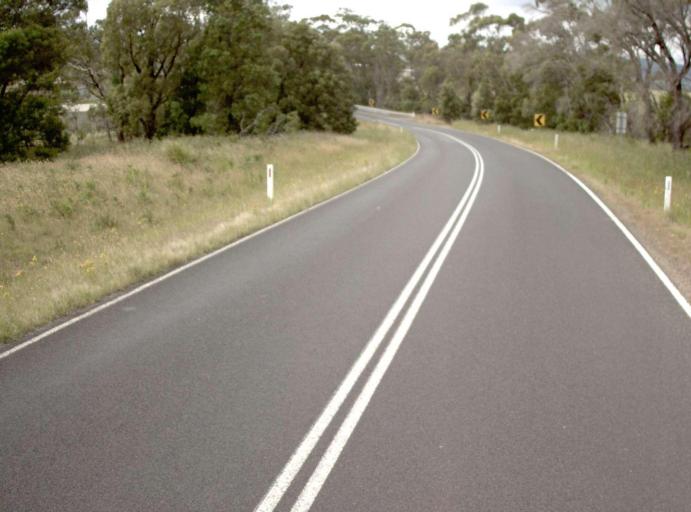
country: AU
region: Victoria
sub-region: Latrobe
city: Moe
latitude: -38.1034
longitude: 146.2379
